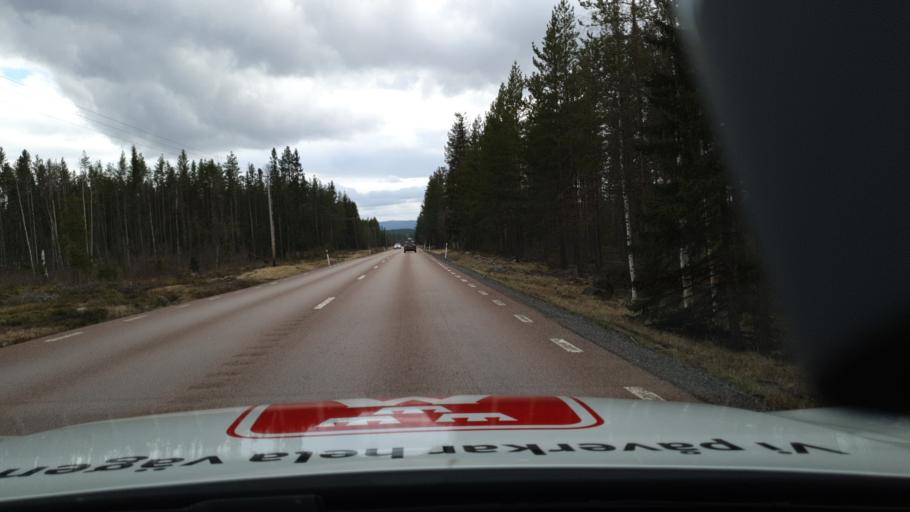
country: SE
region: Vaesternorrland
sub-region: Solleftea Kommun
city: As
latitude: 63.0341
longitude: 16.7192
